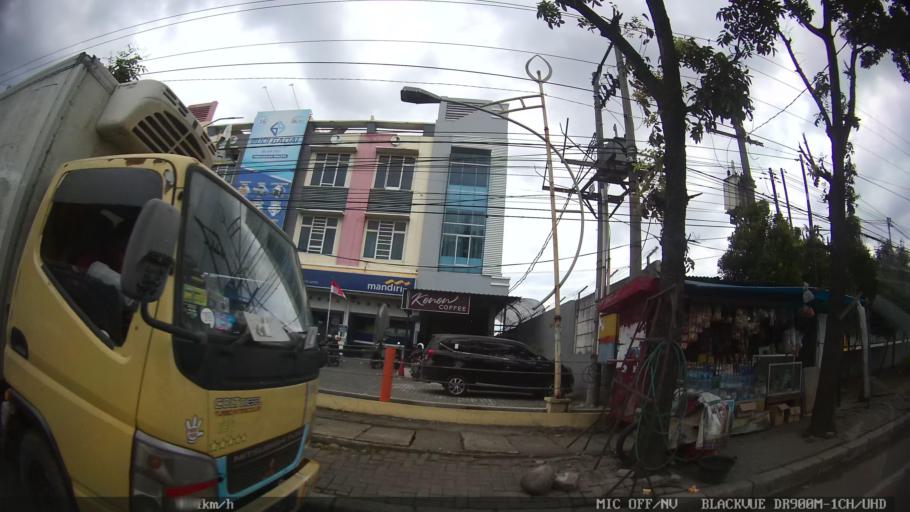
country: ID
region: North Sumatra
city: Sunggal
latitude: 3.5955
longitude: 98.6148
